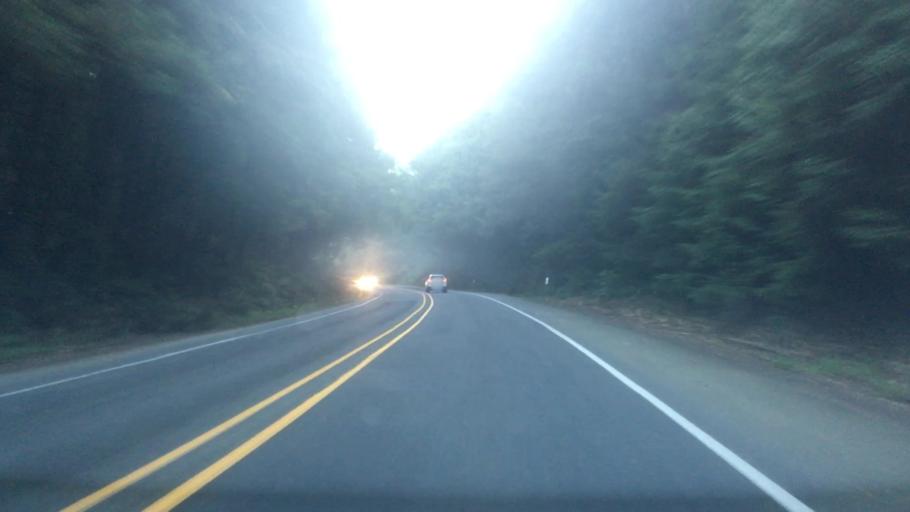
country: US
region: Oregon
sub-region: Clatsop County
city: Cannon Beach
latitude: 45.8848
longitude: -123.9592
